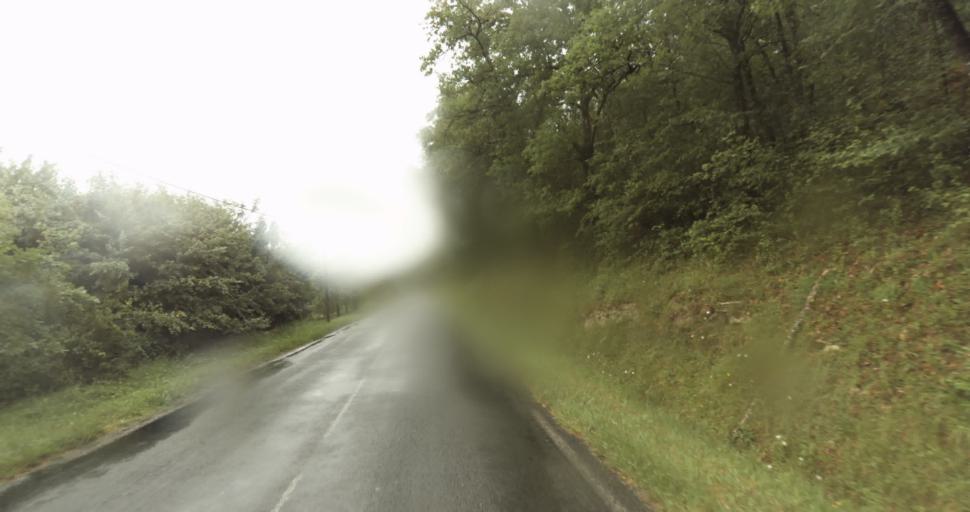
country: FR
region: Aquitaine
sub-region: Departement de la Dordogne
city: Le Bugue
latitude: 44.8325
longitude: 0.8984
